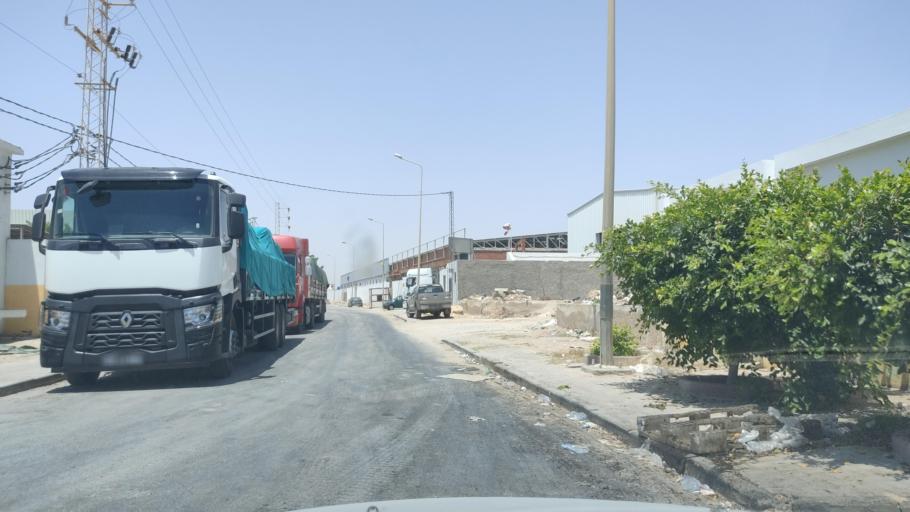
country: TN
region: Safaqis
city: Sfax
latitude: 34.6626
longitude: 10.7007
